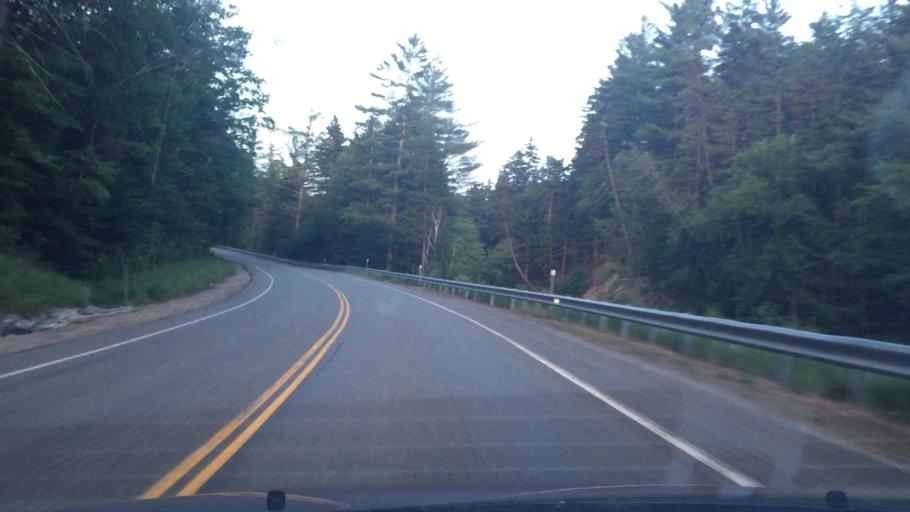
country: US
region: New Hampshire
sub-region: Grafton County
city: Woodstock
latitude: 44.0381
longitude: -71.5380
